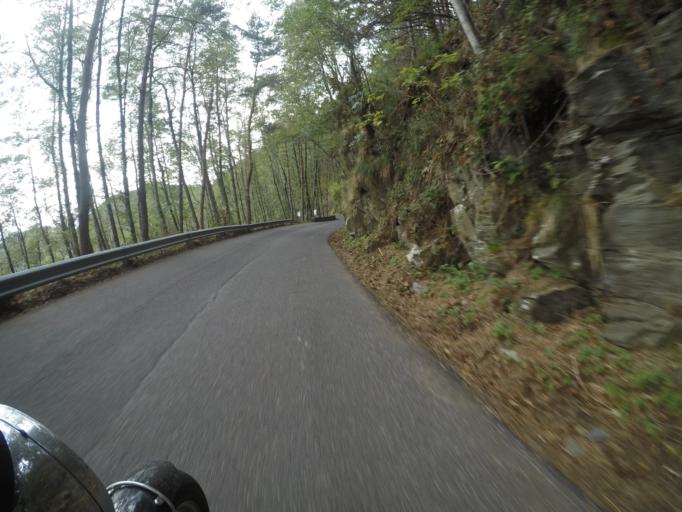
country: IT
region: Tuscany
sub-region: Provincia di Massa-Carrara
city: Carrara
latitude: 44.1219
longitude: 10.1147
